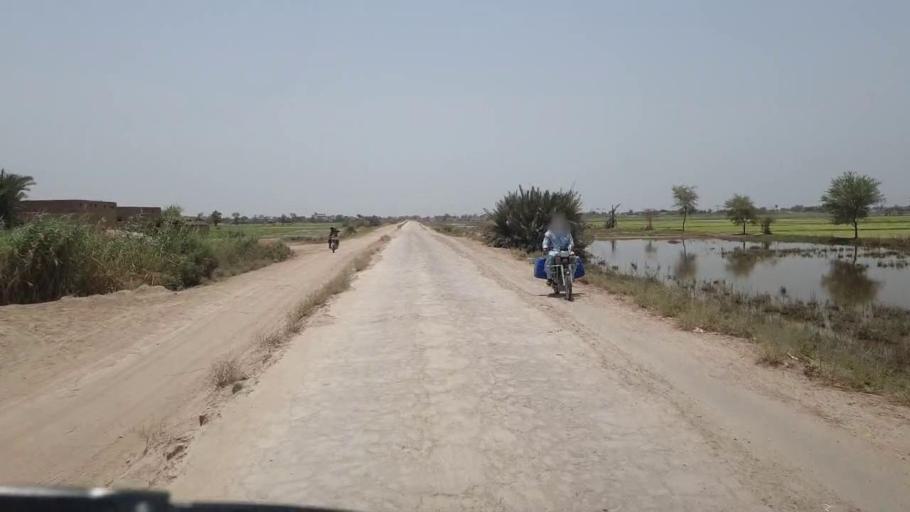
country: PK
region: Sindh
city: Daur
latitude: 26.4607
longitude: 68.1481
